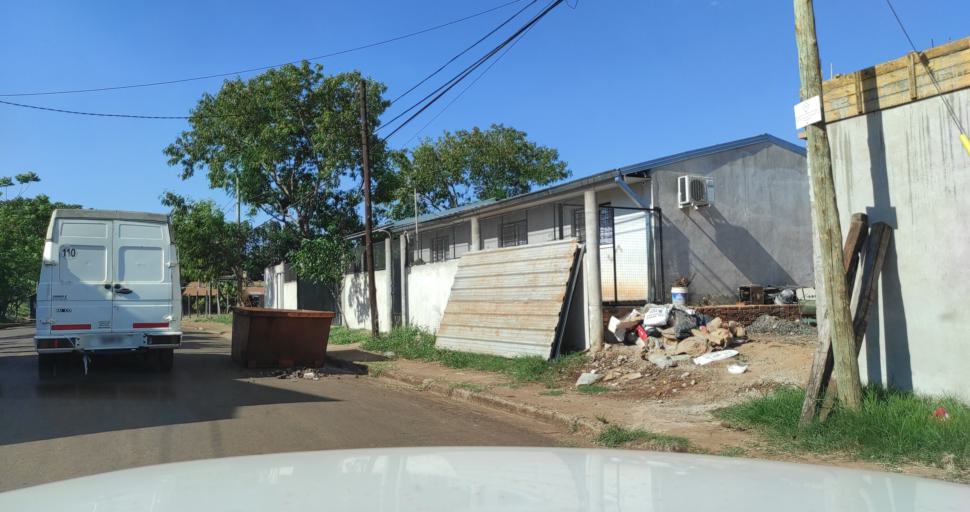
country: AR
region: Misiones
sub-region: Departamento de Capital
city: Posadas
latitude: -27.4130
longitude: -55.9224
